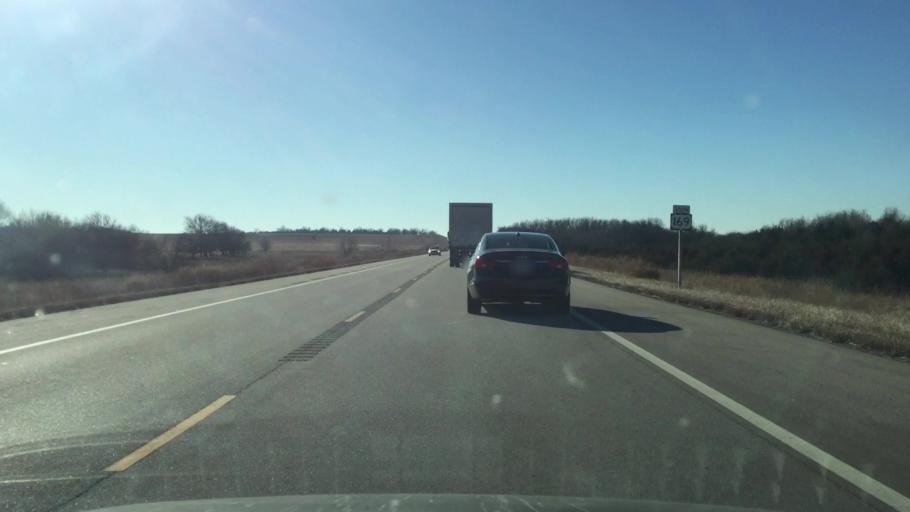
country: US
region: Kansas
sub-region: Allen County
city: Iola
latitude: 38.0236
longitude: -95.3807
